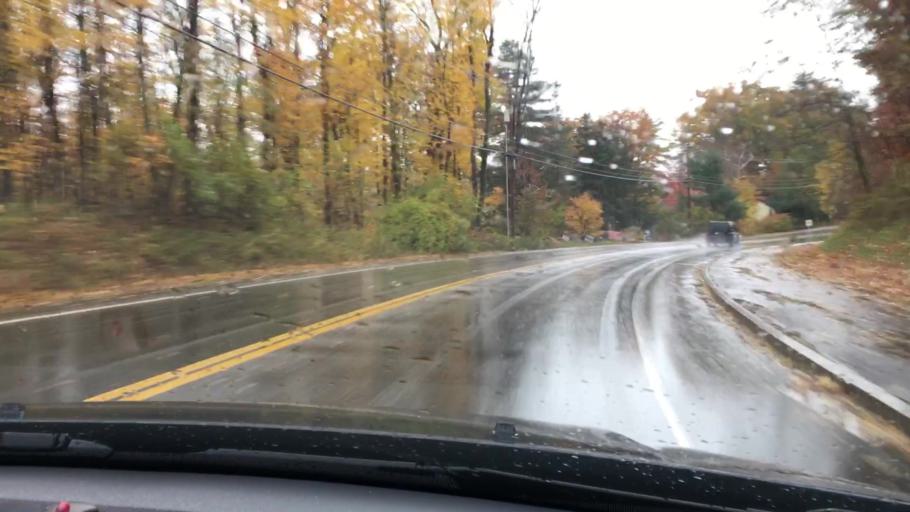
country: US
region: New Hampshire
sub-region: Grafton County
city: Holderness
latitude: 43.7295
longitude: -71.5938
